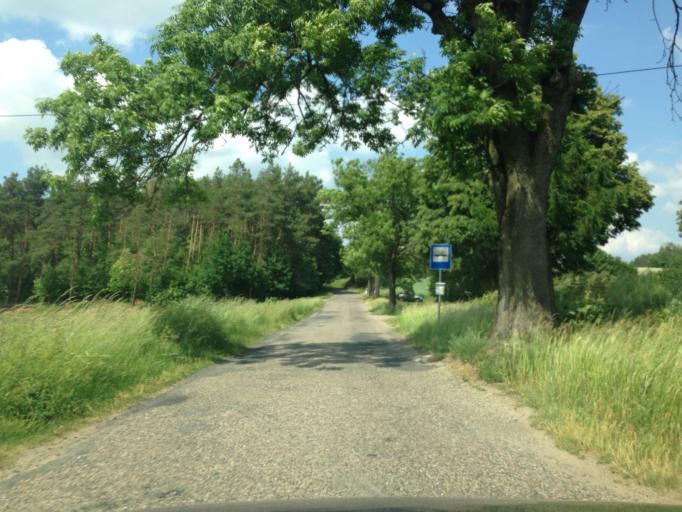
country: PL
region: Kujawsko-Pomorskie
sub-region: Powiat brodnicki
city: Gorzno
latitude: 53.2679
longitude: 19.6906
